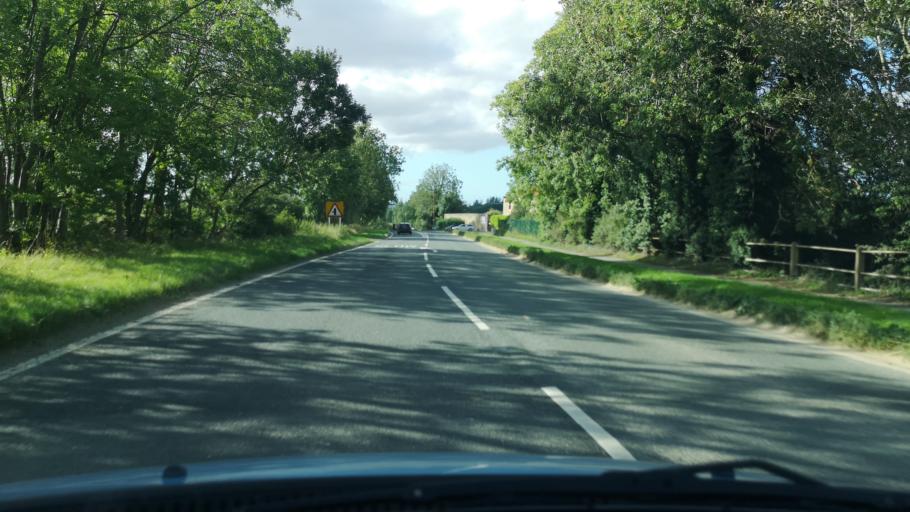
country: GB
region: England
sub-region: City and Borough of Wakefield
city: South Elmsall
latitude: 53.5869
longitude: -1.2408
